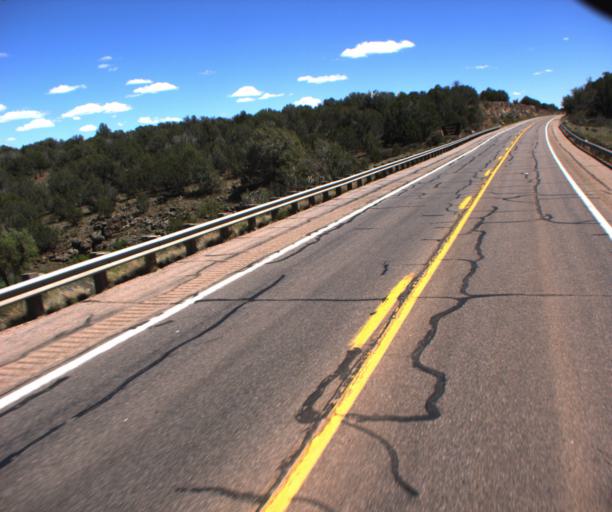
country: US
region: Arizona
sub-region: Yavapai County
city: Paulden
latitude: 35.0814
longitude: -112.4053
